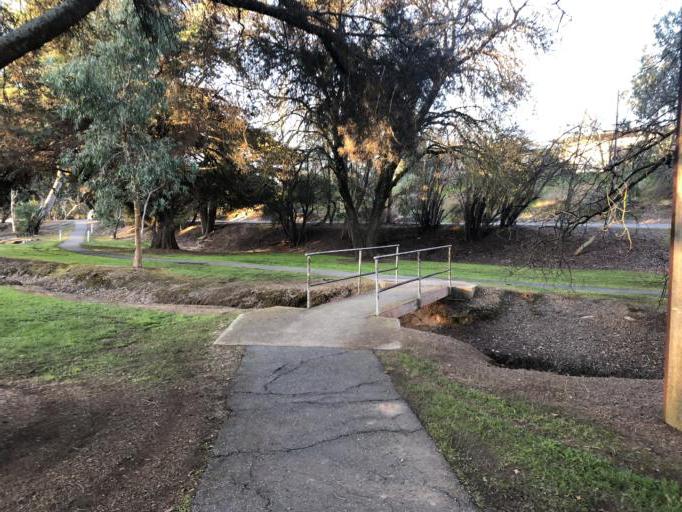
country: AU
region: South Australia
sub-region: Clare and Gilbert Valleys
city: Clare
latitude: -33.8422
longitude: 138.6128
